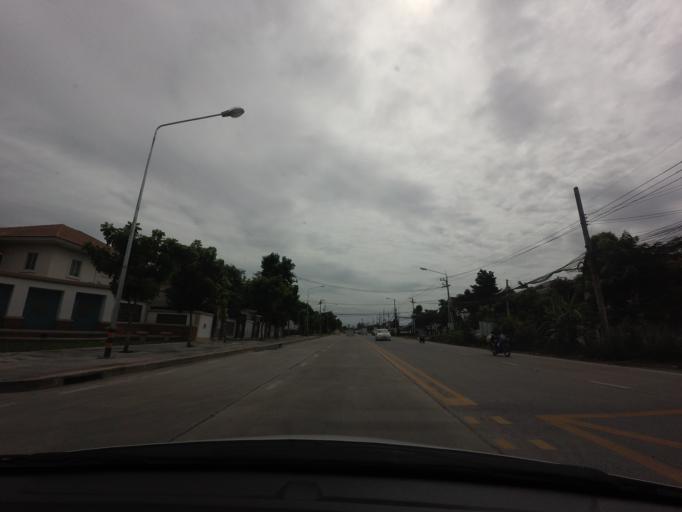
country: TH
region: Pathum Thani
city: Lam Luk Ka
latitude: 13.9293
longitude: 100.7194
